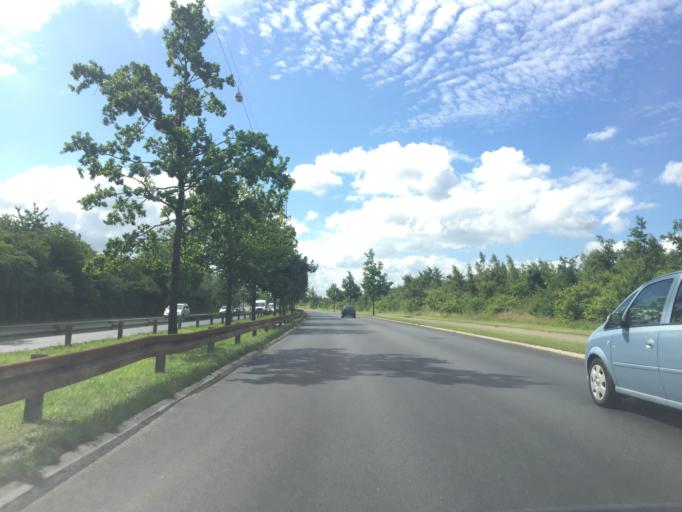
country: DK
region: Capital Region
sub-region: Hvidovre Kommune
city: Hvidovre
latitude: 55.6567
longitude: 12.4545
